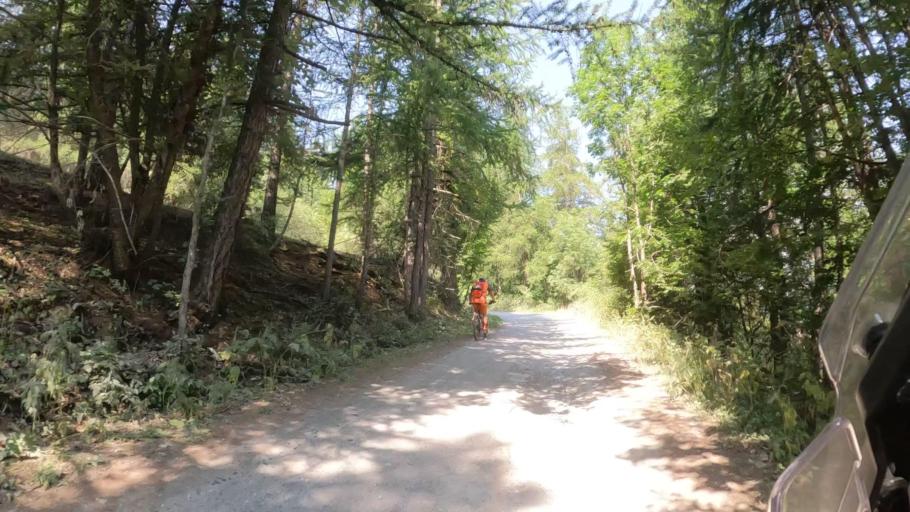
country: IT
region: Piedmont
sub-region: Provincia di Torino
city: Cesana Torinese
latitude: 44.9326
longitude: 6.8133
